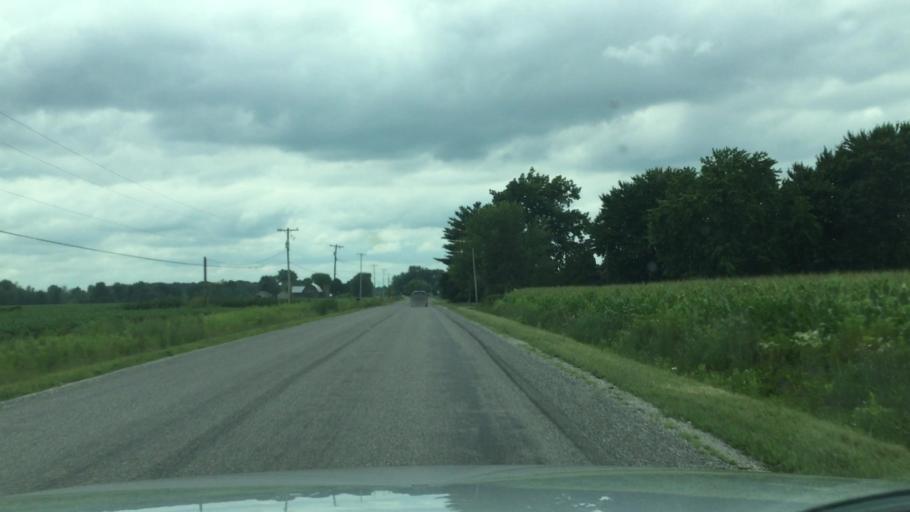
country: US
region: Michigan
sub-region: Saginaw County
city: Birch Run
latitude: 43.2509
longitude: -83.8382
